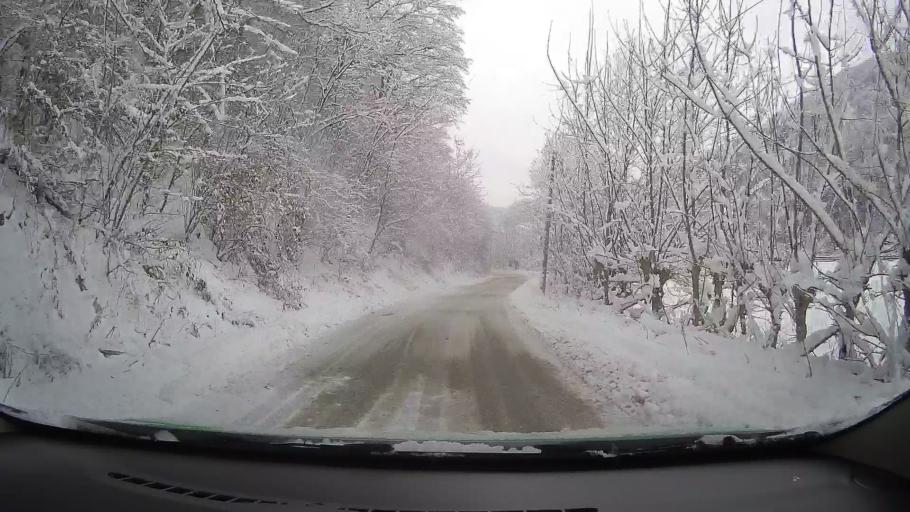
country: RO
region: Alba
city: Pianu de Sus
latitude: 45.8631
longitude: 23.4983
